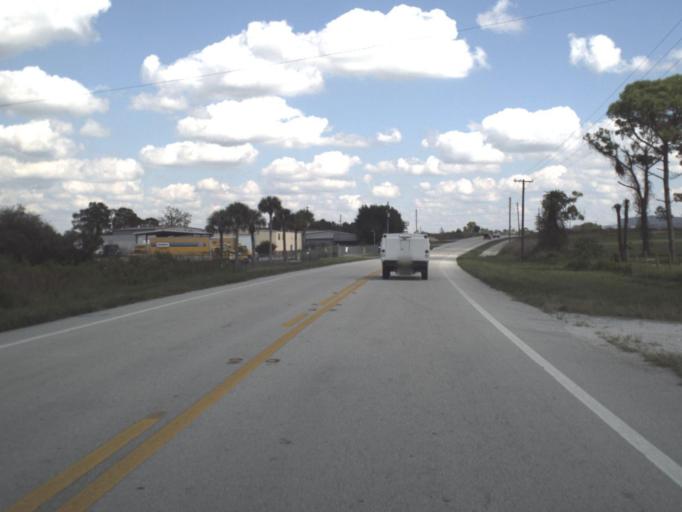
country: US
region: Florida
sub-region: Highlands County
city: Sebring
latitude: 27.4264
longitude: -81.4285
